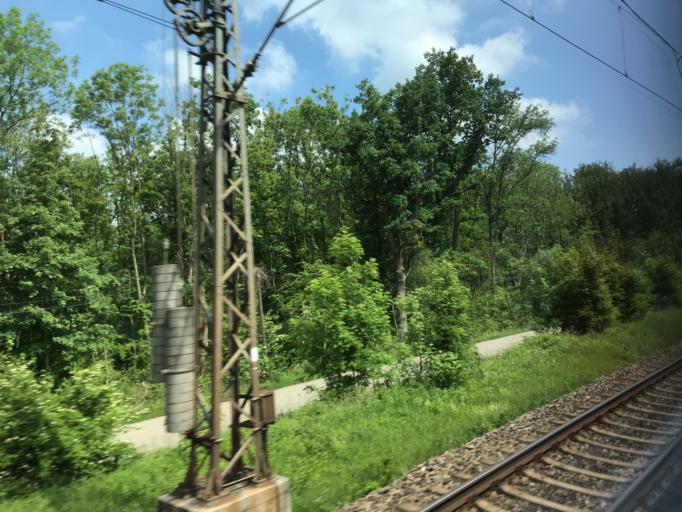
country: DE
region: Bavaria
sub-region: Swabia
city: Offingen
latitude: 48.4875
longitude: 10.3545
